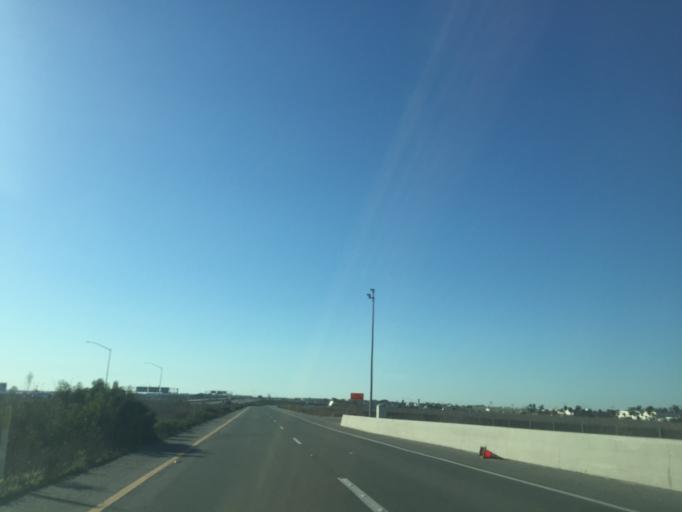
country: MX
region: Baja California
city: Tijuana
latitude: 32.5648
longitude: -116.9521
